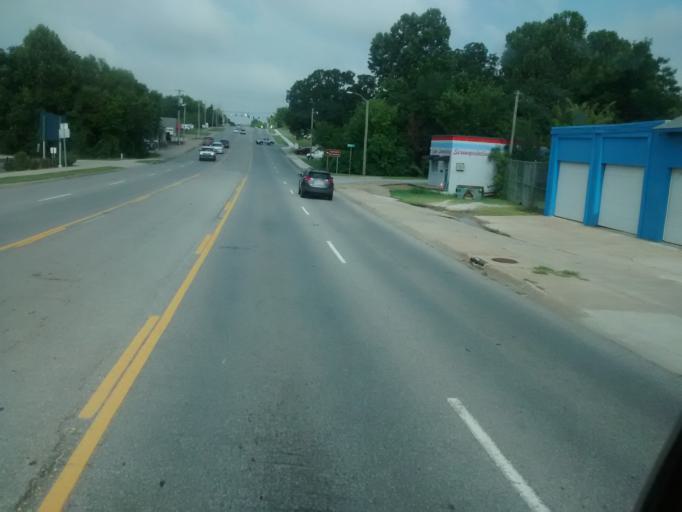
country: US
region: Arkansas
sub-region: Washington County
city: Fayetteville
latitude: 36.0565
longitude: -94.1648
